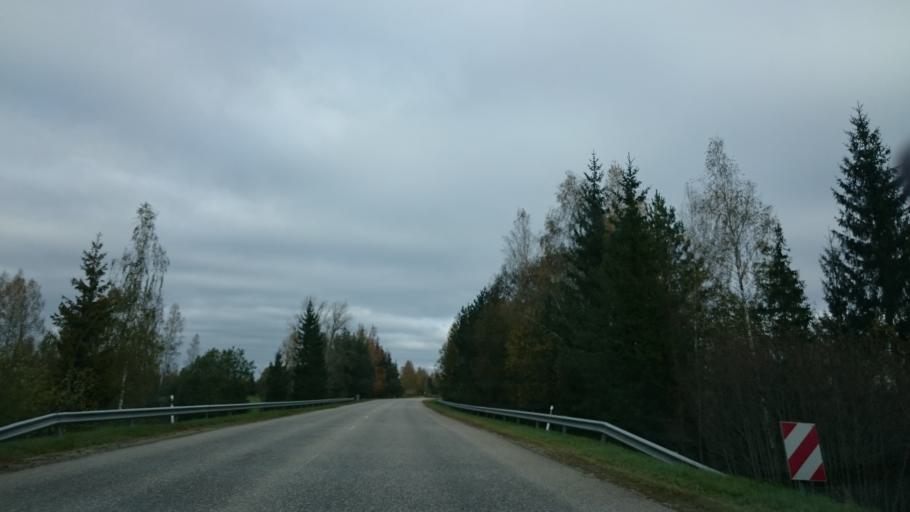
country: LV
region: Amatas Novads
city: Drabesi
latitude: 57.2316
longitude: 25.2538
